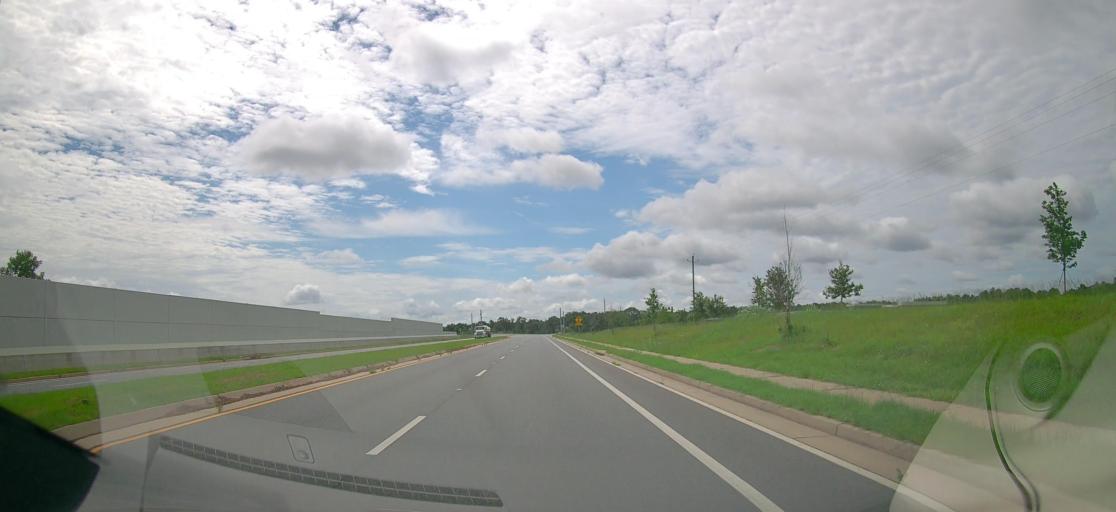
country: US
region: Georgia
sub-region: Houston County
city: Centerville
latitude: 32.7123
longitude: -83.6982
